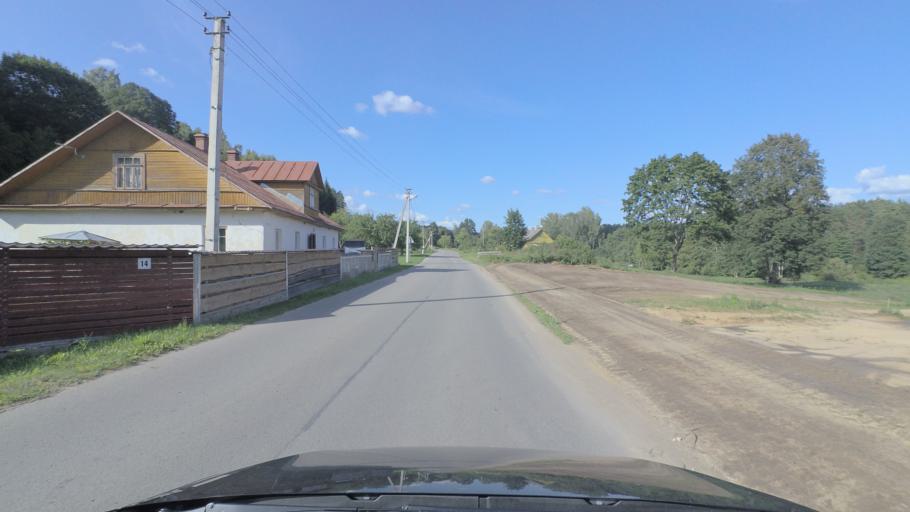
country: LT
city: Nemencine
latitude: 54.8456
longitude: 25.3730
